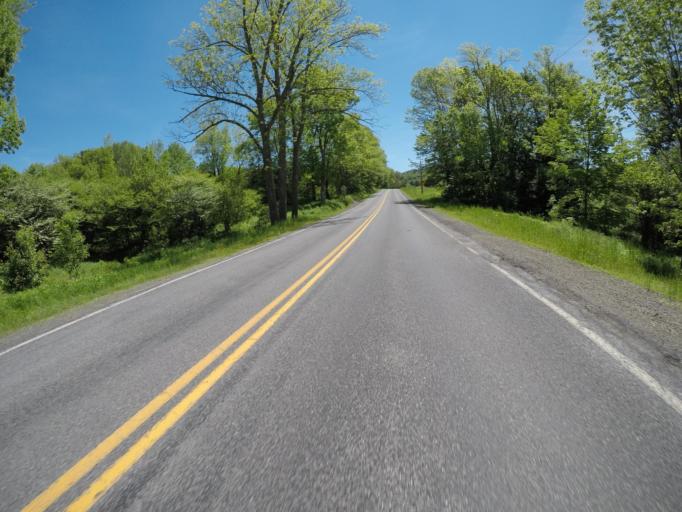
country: US
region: New York
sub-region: Delaware County
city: Delhi
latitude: 42.2095
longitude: -74.8590
